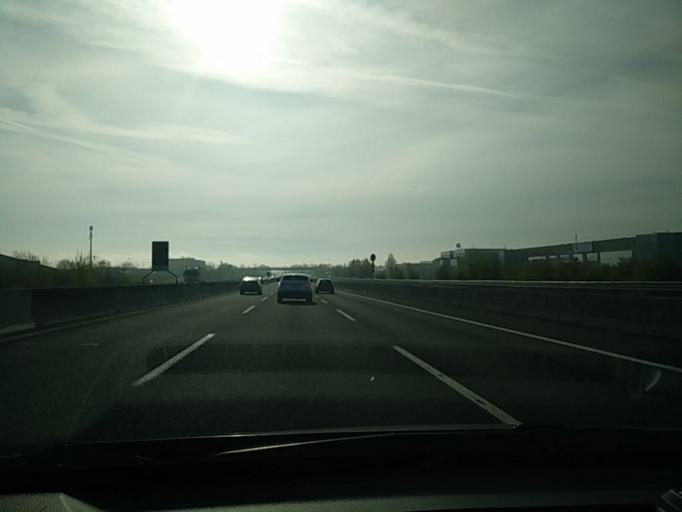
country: IT
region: Emilia-Romagna
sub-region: Provincia di Bologna
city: Ozzano dell'Emilia
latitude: 44.4629
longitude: 11.4966
